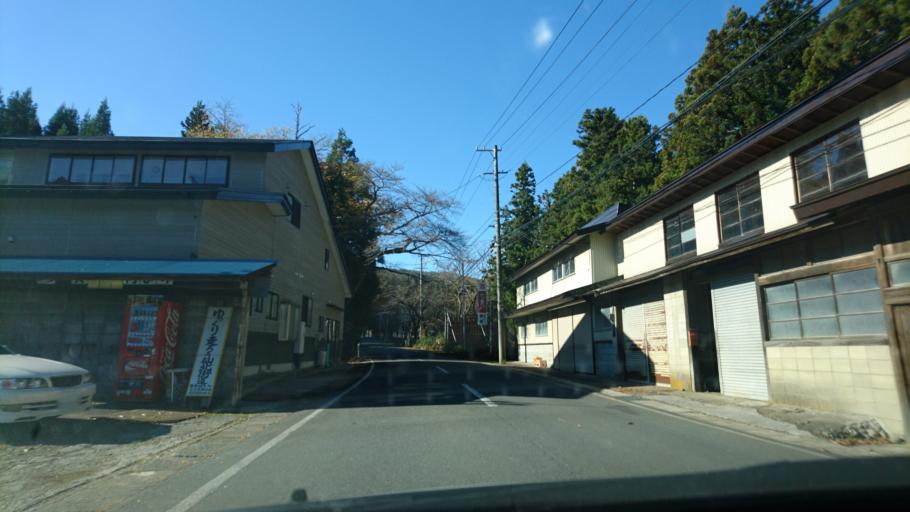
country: JP
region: Iwate
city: Mizusawa
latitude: 39.1172
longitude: 140.9492
